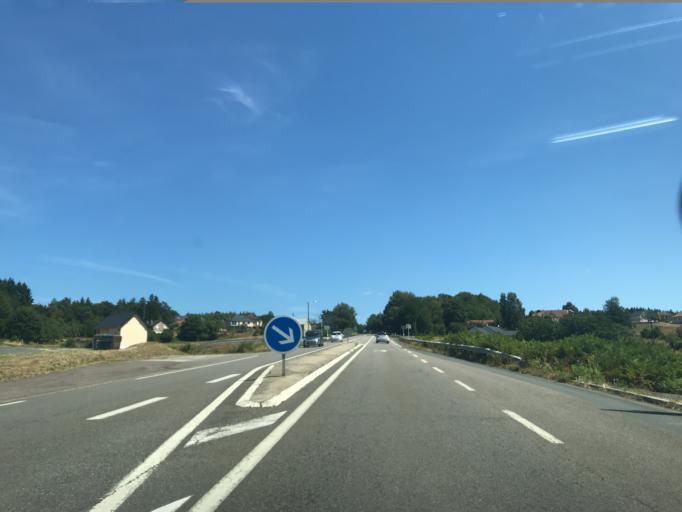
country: FR
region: Limousin
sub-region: Departement de la Correze
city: Correze
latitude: 45.3177
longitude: 1.8391
